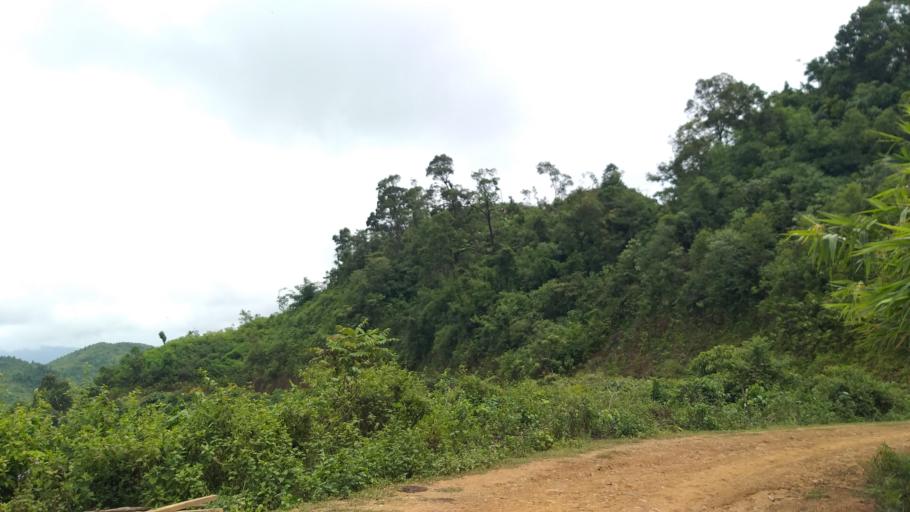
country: LA
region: Phongsali
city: Khoa
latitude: 21.3938
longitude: 102.6650
